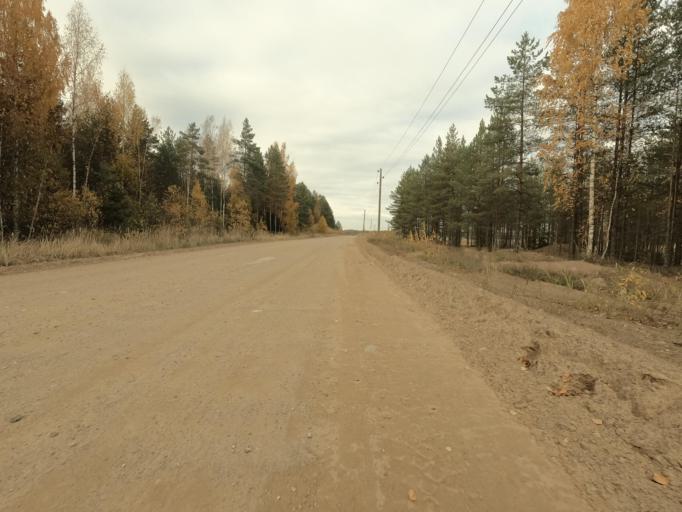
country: RU
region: Leningrad
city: Priladozhskiy
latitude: 59.6975
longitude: 31.3620
